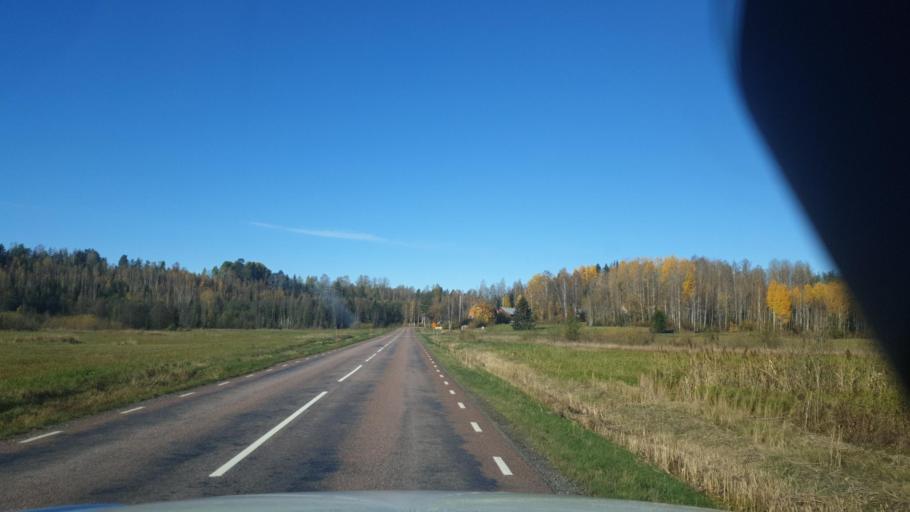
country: SE
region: Vaermland
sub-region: Grums Kommun
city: Slottsbron
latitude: 59.4246
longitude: 12.9798
